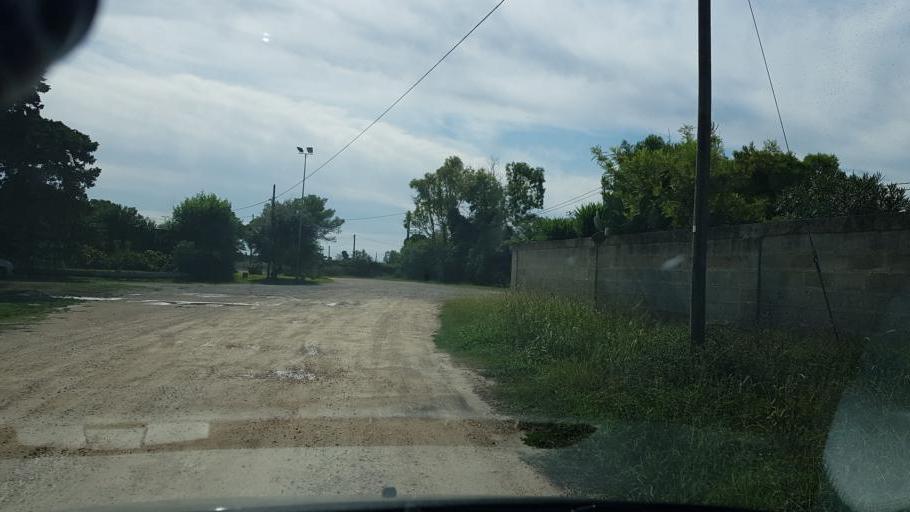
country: IT
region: Apulia
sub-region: Provincia di Lecce
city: Borgagne
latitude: 40.2291
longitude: 18.4418
